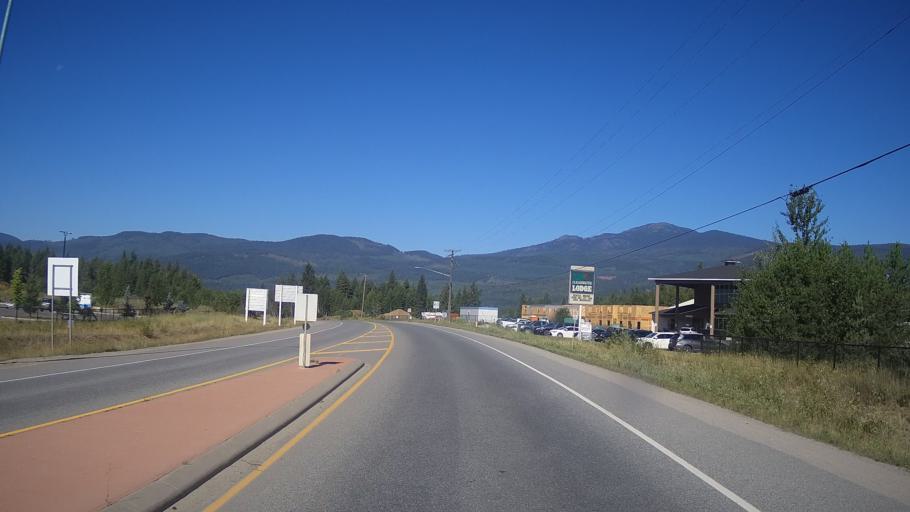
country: CA
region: British Columbia
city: Chase
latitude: 51.6508
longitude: -120.0404
